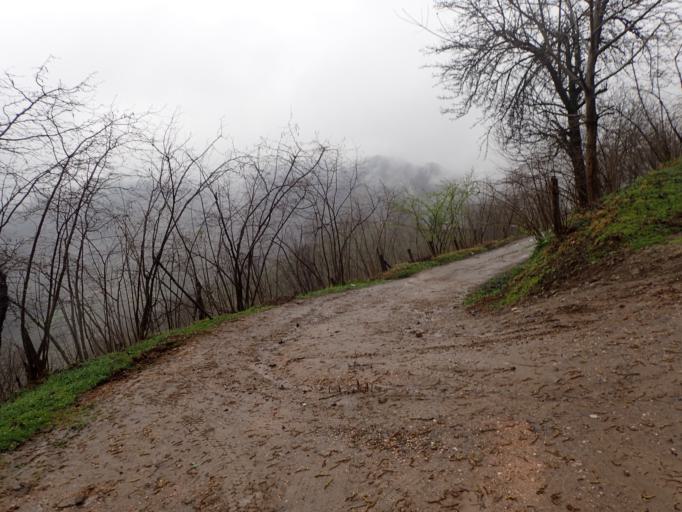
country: TR
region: Ordu
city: Camas
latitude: 40.9136
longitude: 37.5713
